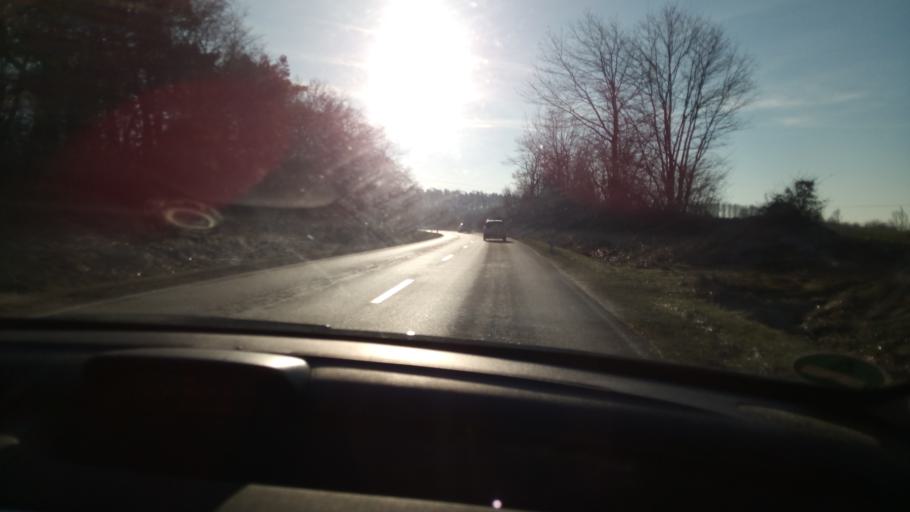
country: DE
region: Schleswig-Holstein
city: Buchhorst
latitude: 53.3960
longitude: 10.5558
